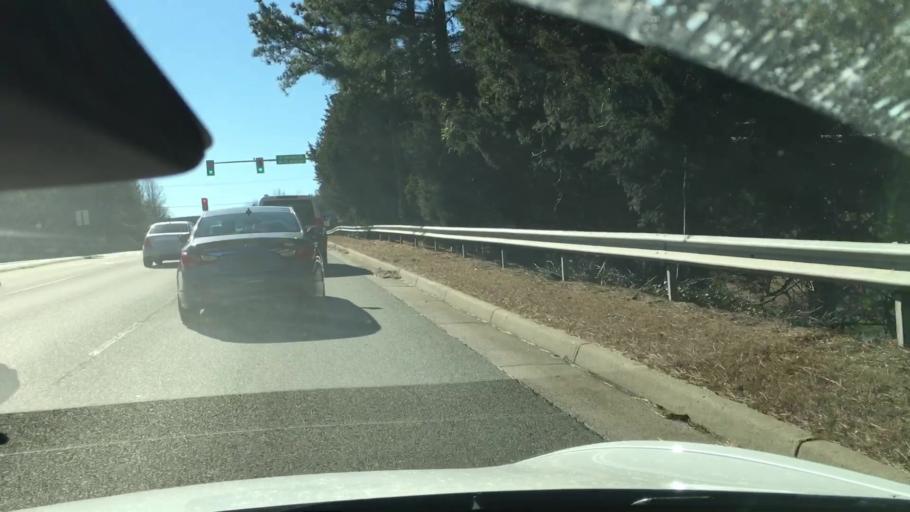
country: US
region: Virginia
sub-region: Henrico County
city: Tuckahoe
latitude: 37.5732
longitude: -77.5754
